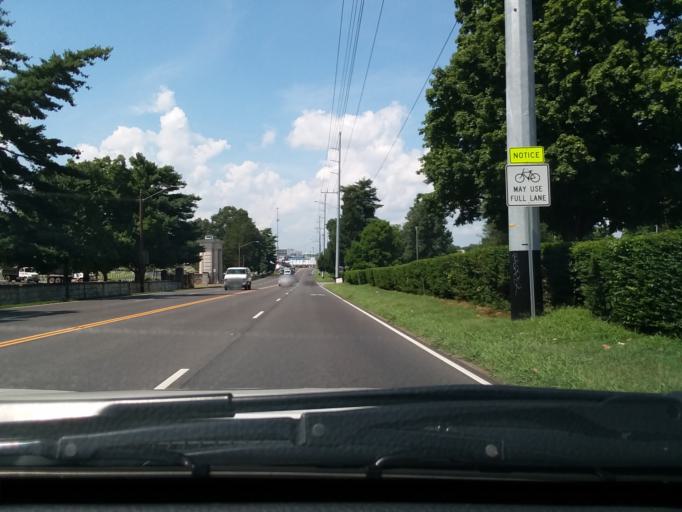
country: US
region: Tennessee
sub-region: Davidson County
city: Goodlettsville
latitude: 36.2405
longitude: -86.7234
